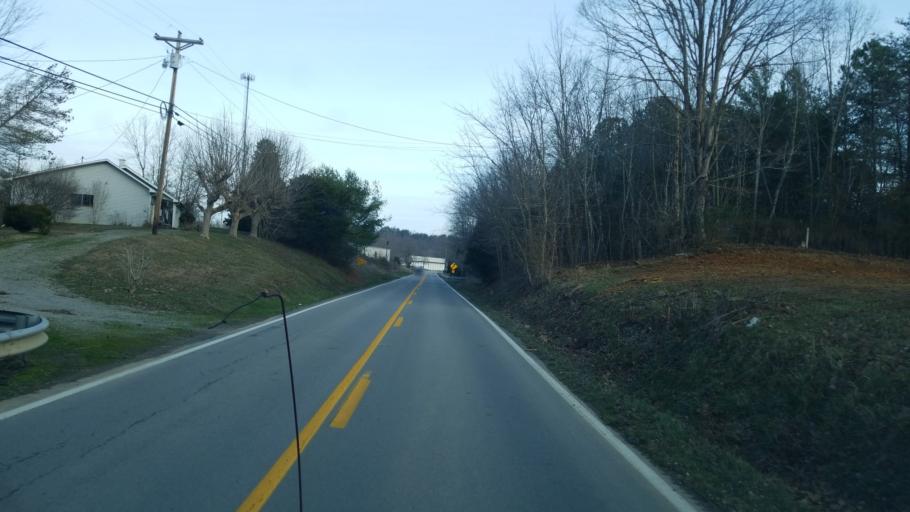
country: US
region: Kentucky
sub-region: Russell County
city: Jamestown
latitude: 36.8816
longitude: -85.1010
